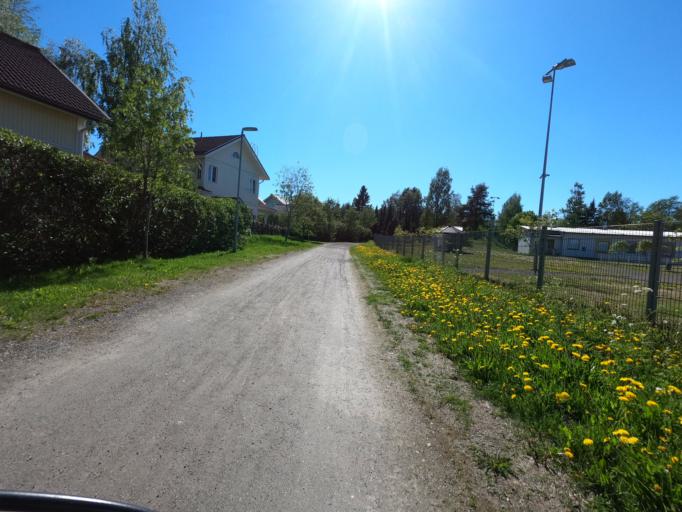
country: FI
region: North Karelia
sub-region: Joensuu
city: Joensuu
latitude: 62.5936
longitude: 29.7943
